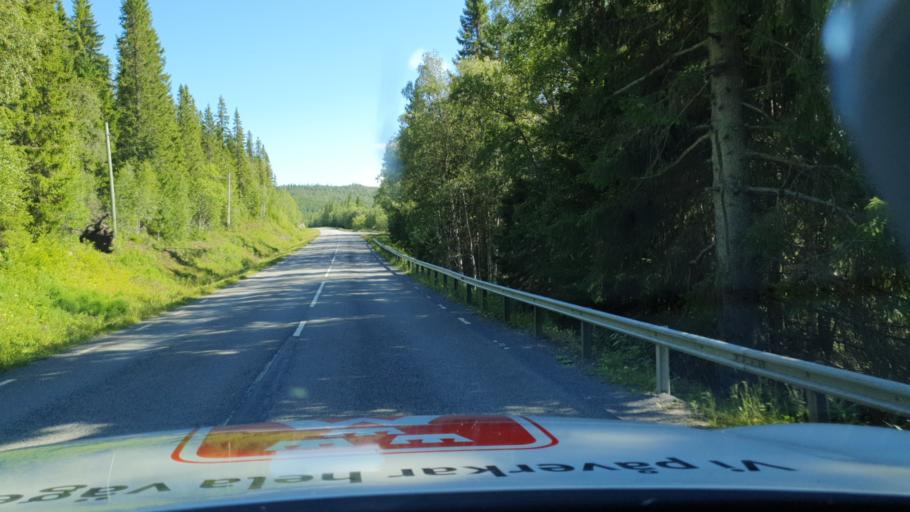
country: SE
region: Jaemtland
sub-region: Are Kommun
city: Are
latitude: 63.4986
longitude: 13.1690
